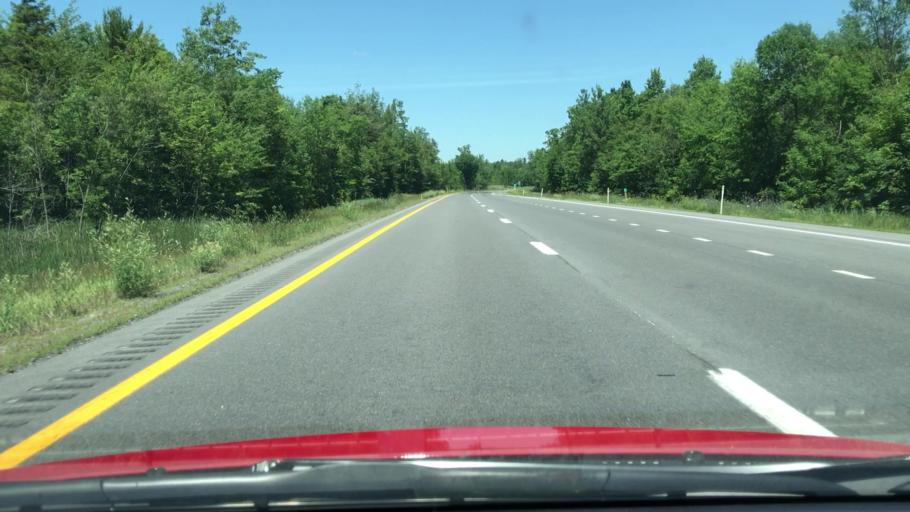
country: US
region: New York
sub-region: Clinton County
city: Champlain
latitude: 44.8932
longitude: -73.4539
